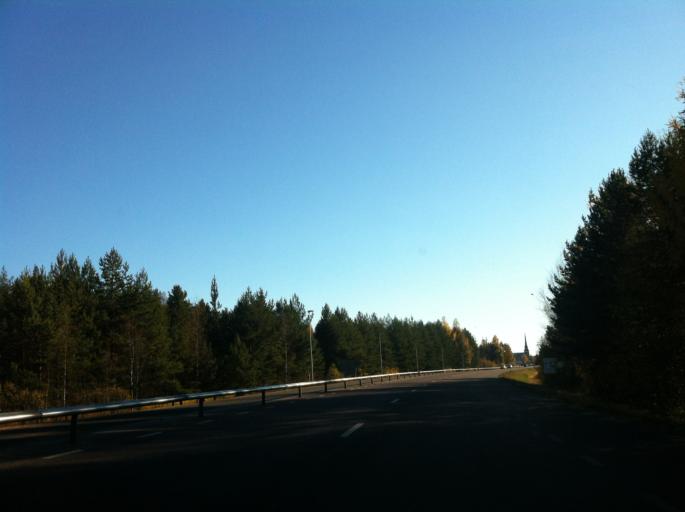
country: SE
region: Dalarna
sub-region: Mora Kommun
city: Mora
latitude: 61.0229
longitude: 14.5356
